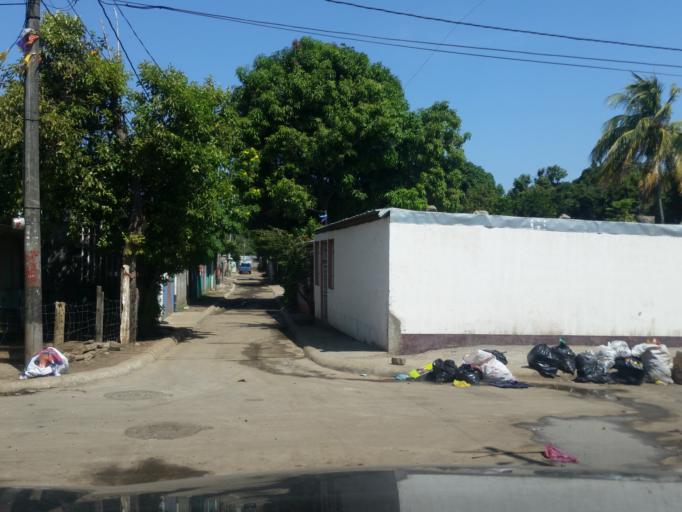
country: NI
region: Managua
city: Managua
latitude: 12.1282
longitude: -86.2779
